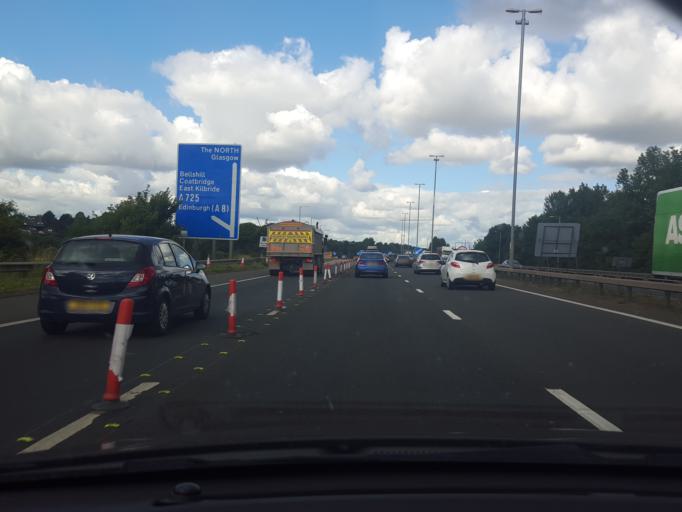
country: GB
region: Scotland
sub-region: South Lanarkshire
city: Bothwell
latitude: 55.7980
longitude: -4.0483
